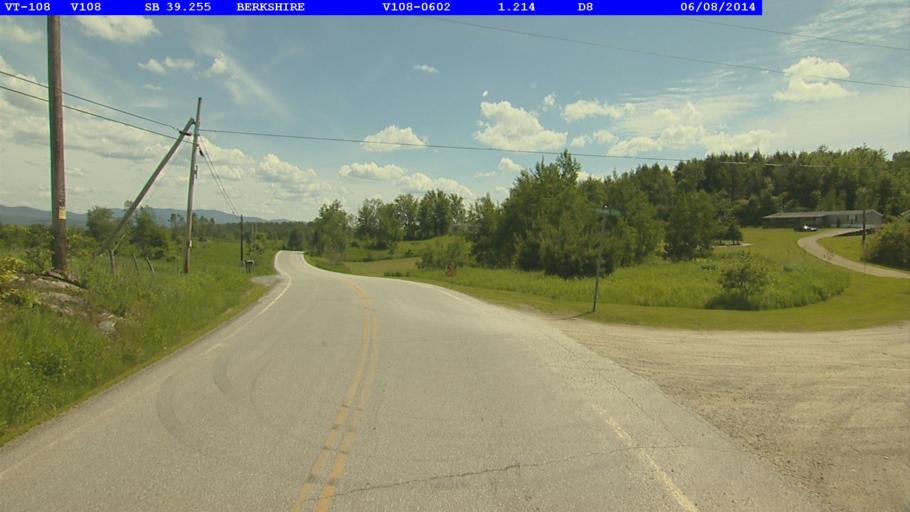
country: US
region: Vermont
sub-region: Franklin County
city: Enosburg Falls
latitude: 44.9421
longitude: -72.8138
